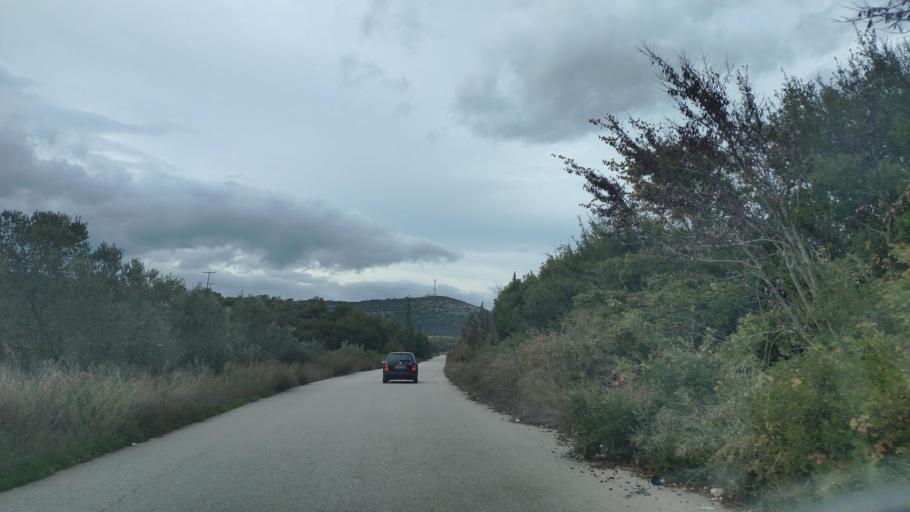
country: GR
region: Peloponnese
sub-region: Nomos Korinthias
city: Ayios Vasilios
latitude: 37.7922
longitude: 22.7322
